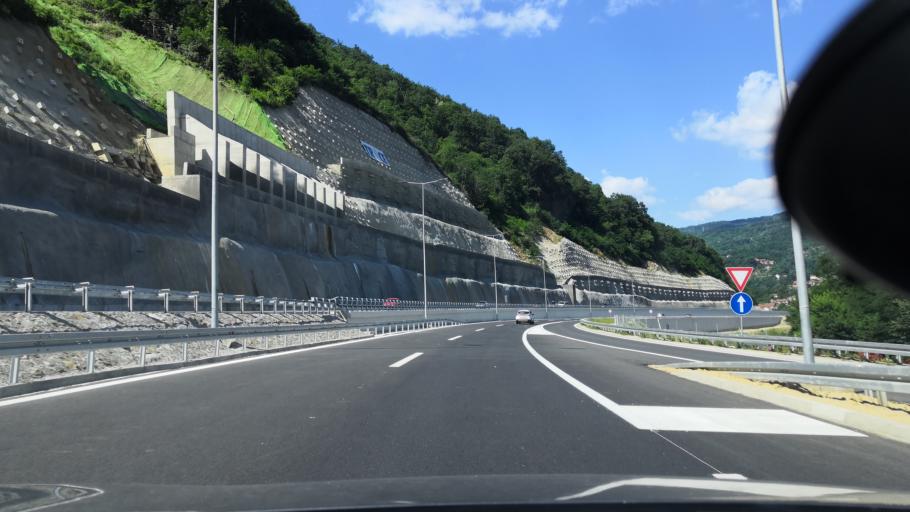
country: RS
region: Central Serbia
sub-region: Pcinjski Okrug
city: Vladicin Han
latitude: 42.8214
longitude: 22.1217
